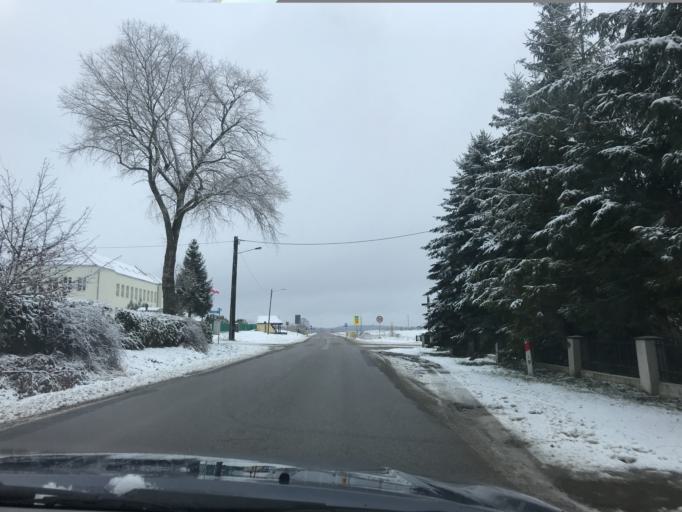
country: PL
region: Pomeranian Voivodeship
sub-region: Powiat bytowski
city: Bytow
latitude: 54.2096
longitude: 17.5465
